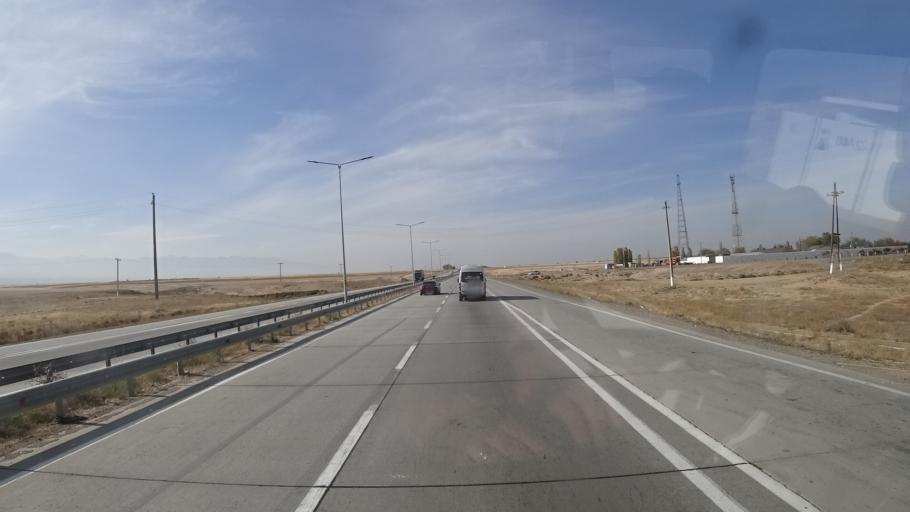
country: KZ
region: Zhambyl
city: Merke
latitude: 42.8894
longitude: 72.9850
